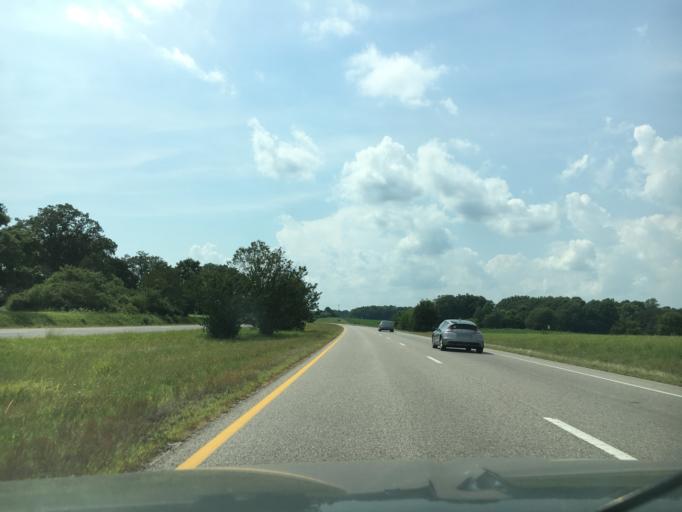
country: US
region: Virginia
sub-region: Amelia County
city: Amelia Court House
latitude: 37.3652
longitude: -77.8977
